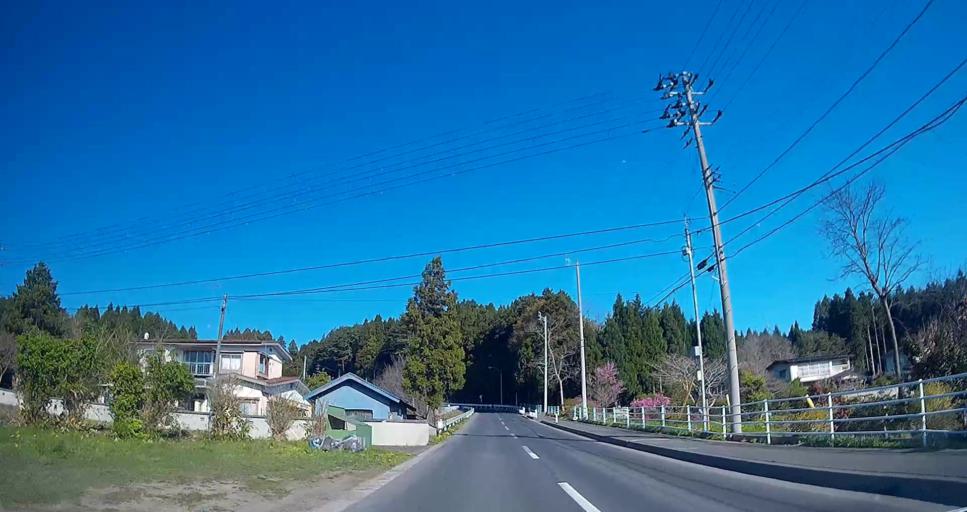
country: JP
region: Aomori
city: Hachinohe
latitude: 40.5189
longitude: 141.5832
